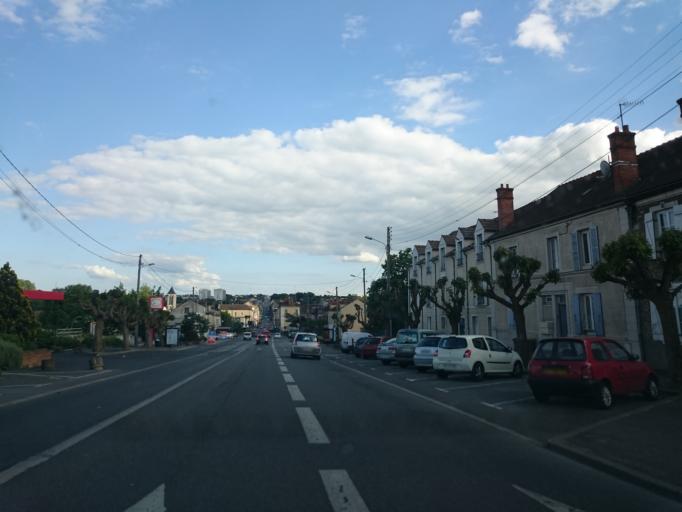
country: FR
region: Ile-de-France
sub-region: Departement de l'Essonne
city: Corbeil-Essonnes
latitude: 48.6068
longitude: 2.4656
